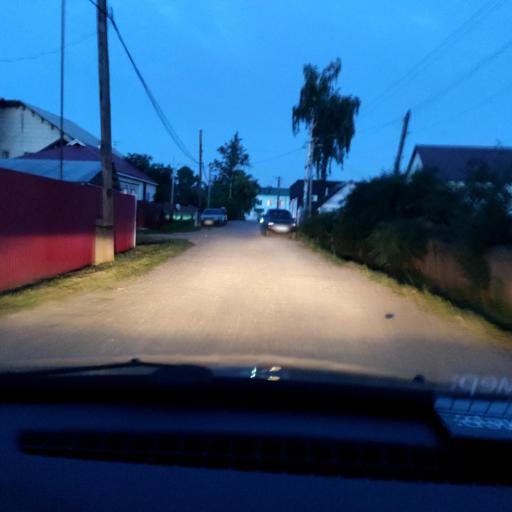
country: RU
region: Bashkortostan
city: Iglino
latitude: 54.8347
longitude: 56.4119
